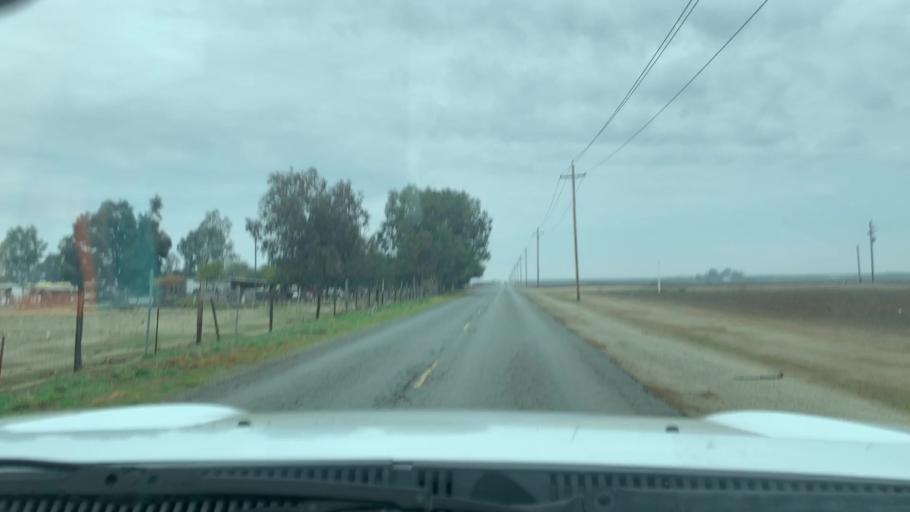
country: US
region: California
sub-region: Tulare County
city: Alpaugh
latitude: 35.7611
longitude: -119.4205
